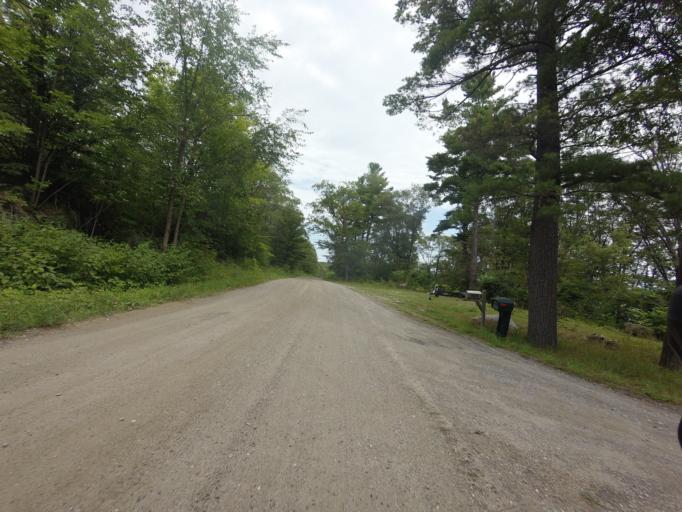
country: CA
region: Ontario
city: Perth
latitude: 44.7257
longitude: -76.6225
